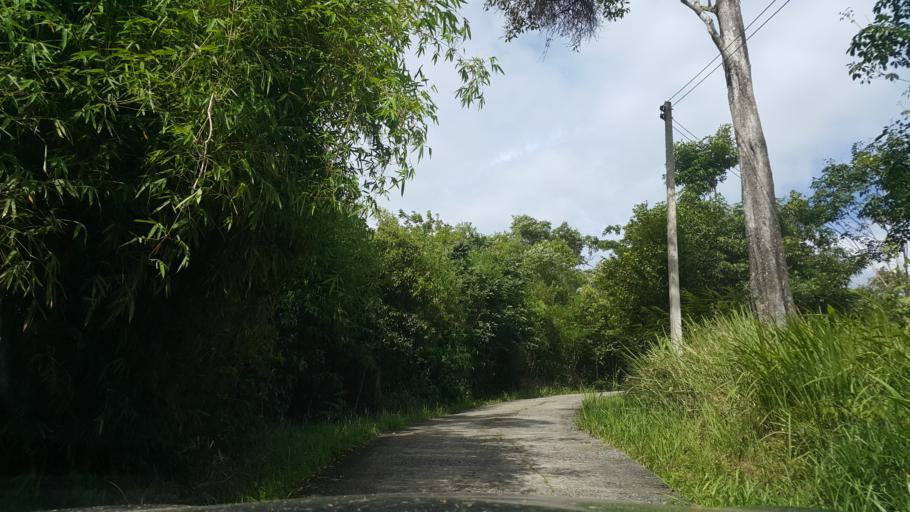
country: TH
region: Loei
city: Na Haeo
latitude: 17.5639
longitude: 100.9493
